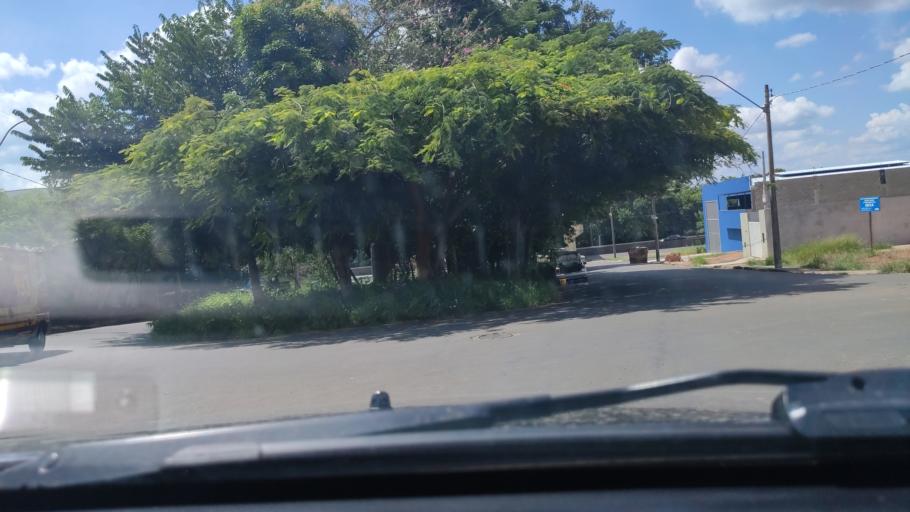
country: BR
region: Sao Paulo
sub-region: Sao Carlos
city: Sao Carlos
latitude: -21.9967
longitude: -47.8779
